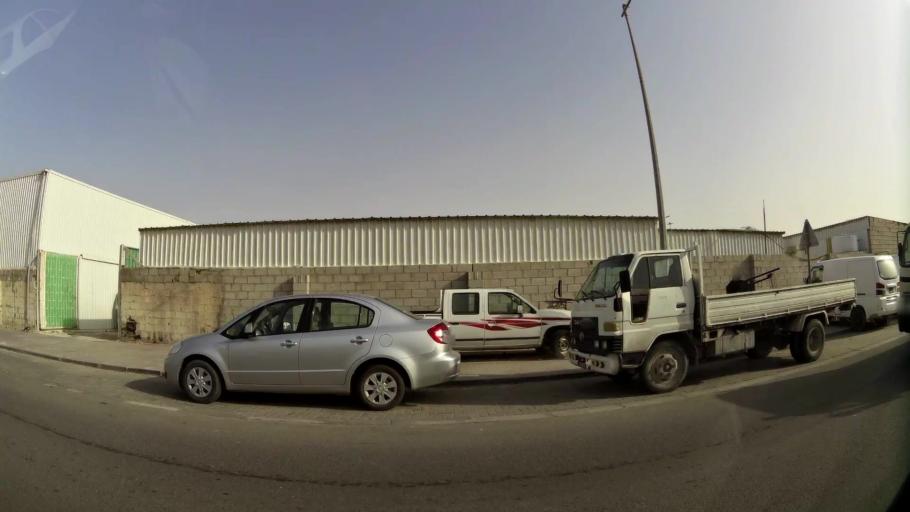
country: QA
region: Baladiyat ar Rayyan
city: Ar Rayyan
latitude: 25.2325
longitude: 51.4411
